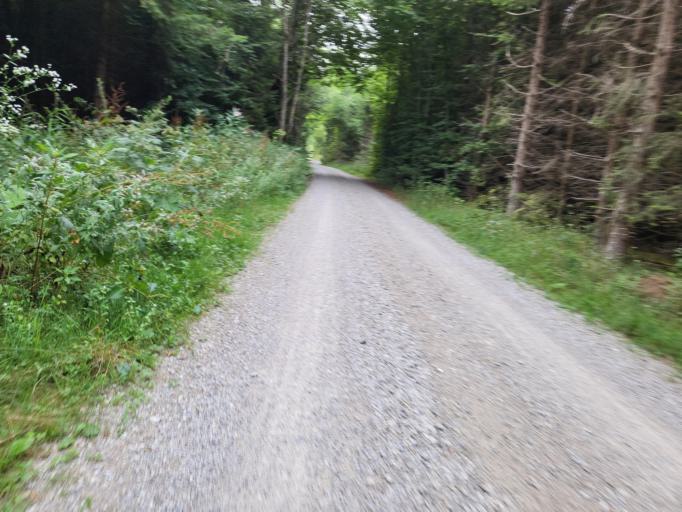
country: DE
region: Bavaria
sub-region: Upper Bavaria
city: Aying
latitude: 47.9853
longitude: 11.7650
